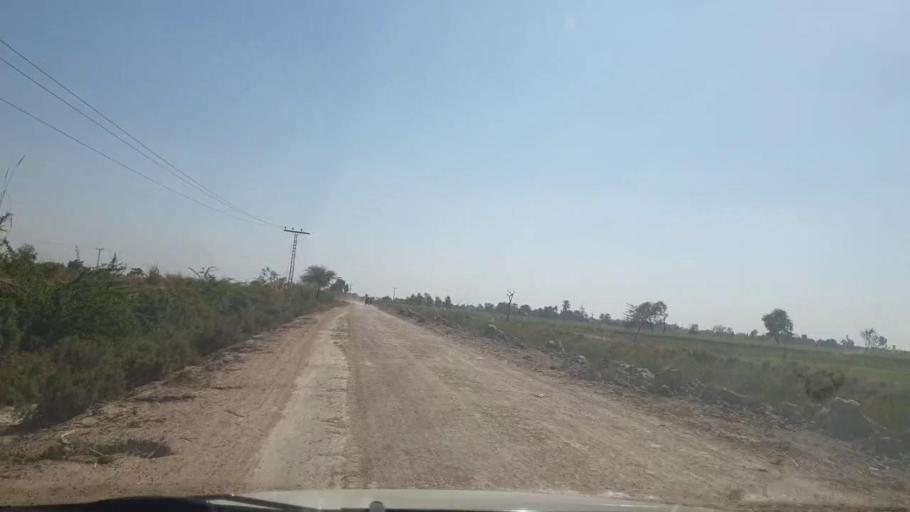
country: PK
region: Sindh
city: Mirpur Khas
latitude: 25.4994
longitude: 69.1358
